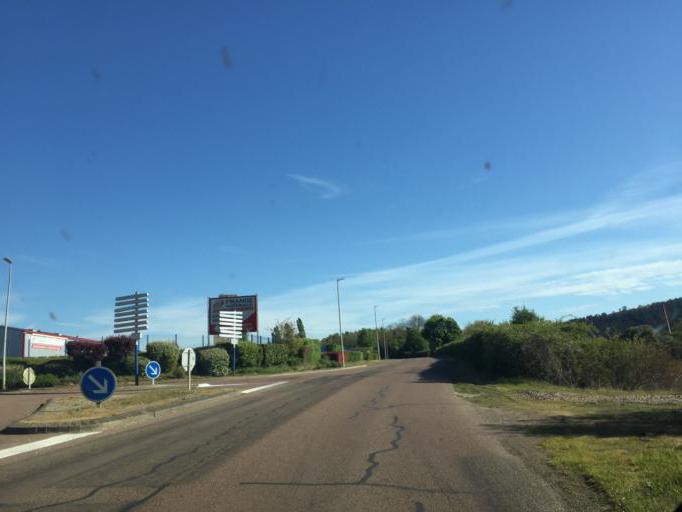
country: FR
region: Bourgogne
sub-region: Departement de la Nievre
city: Clamecy
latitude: 47.4681
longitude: 3.5201
